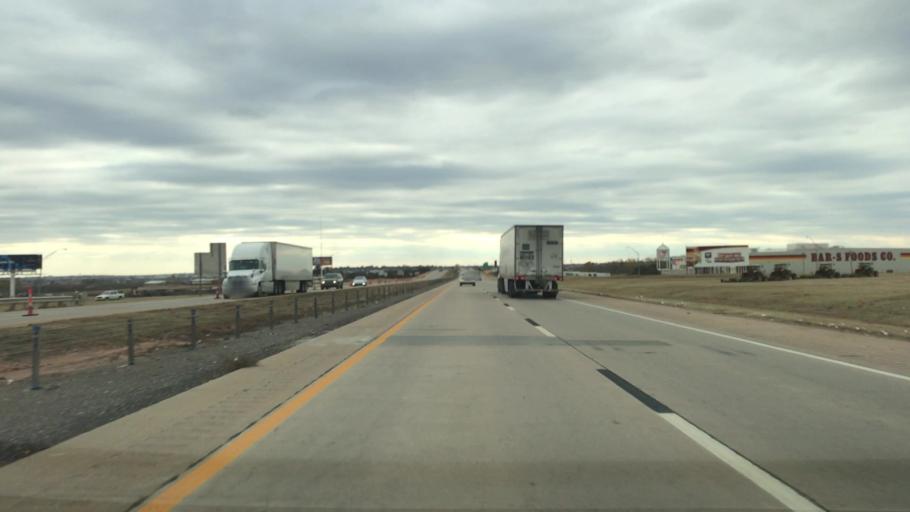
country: US
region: Oklahoma
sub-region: Beckham County
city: Elk City
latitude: 35.4075
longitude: -99.3835
